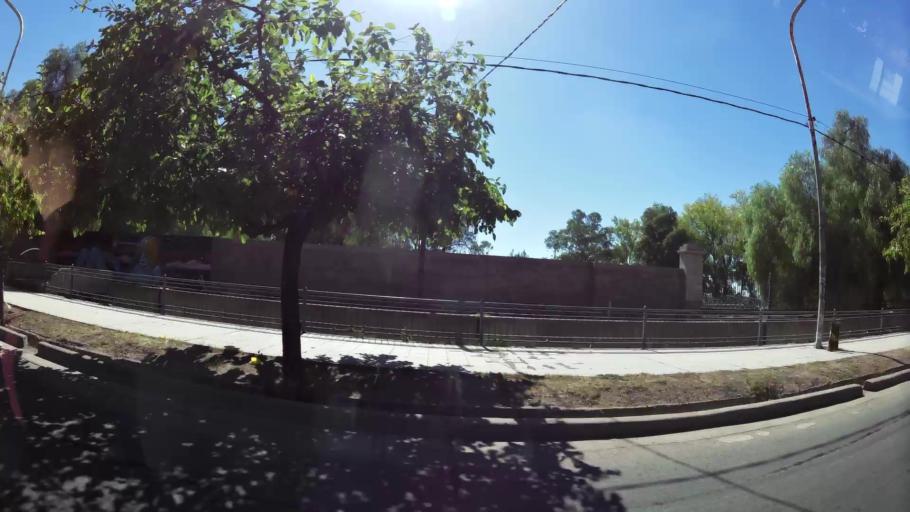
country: AR
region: Mendoza
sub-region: Departamento de Godoy Cruz
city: Godoy Cruz
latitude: -32.9112
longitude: -68.8707
